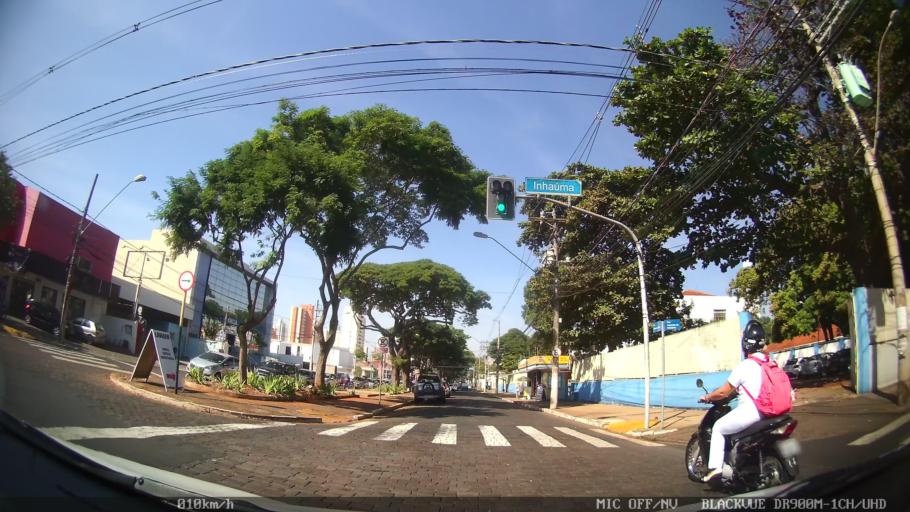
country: BR
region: Sao Paulo
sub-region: Ribeirao Preto
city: Ribeirao Preto
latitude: -21.1829
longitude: -47.8144
